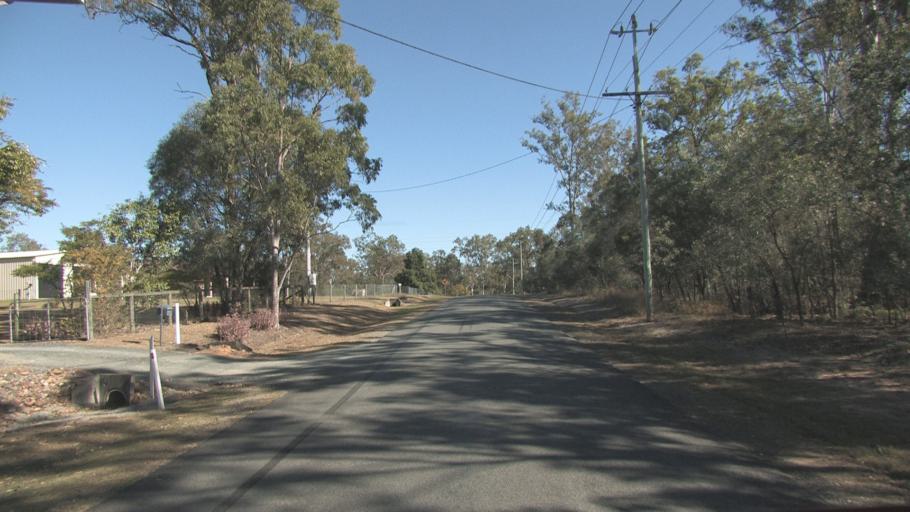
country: AU
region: Queensland
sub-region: Logan
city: North Maclean
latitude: -27.7981
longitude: 153.0433
